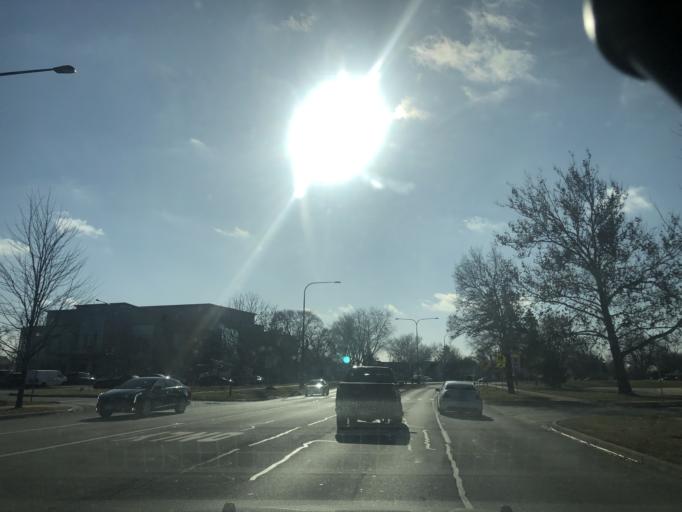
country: US
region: Illinois
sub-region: DuPage County
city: Addison
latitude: 41.9334
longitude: -87.9943
